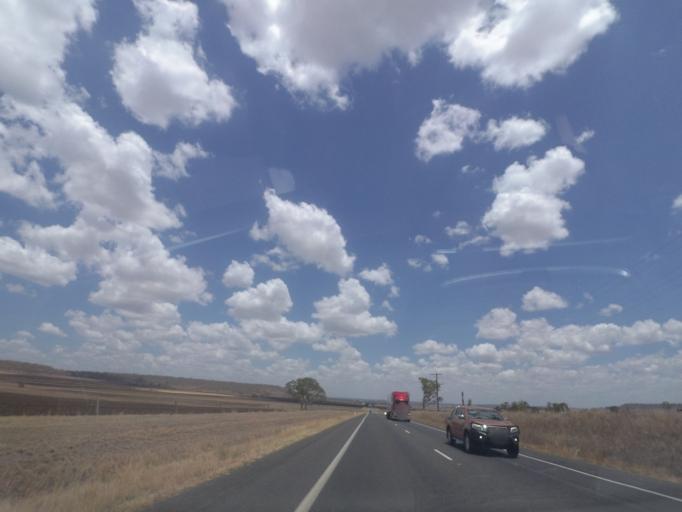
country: AU
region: Queensland
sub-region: Southern Downs
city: Warwick
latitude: -27.9977
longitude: 151.9948
